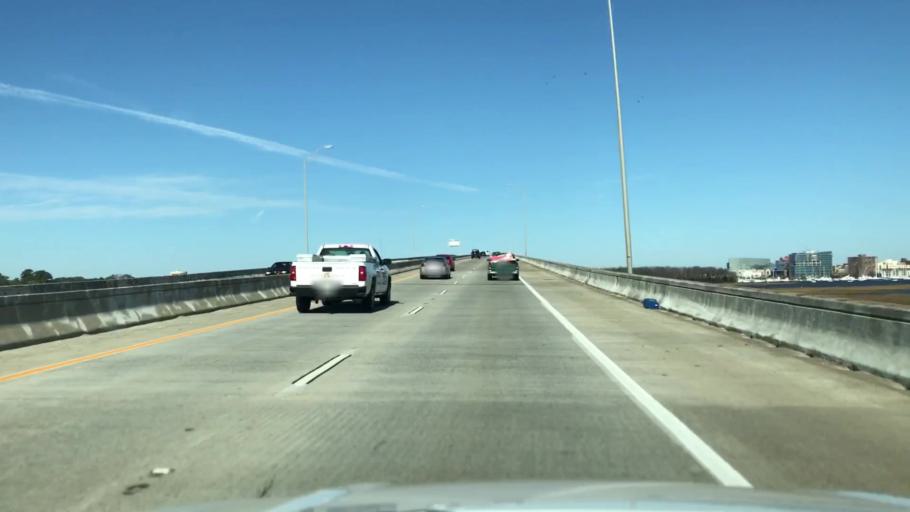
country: US
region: South Carolina
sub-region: Charleston County
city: Charleston
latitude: 32.7653
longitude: -79.9580
